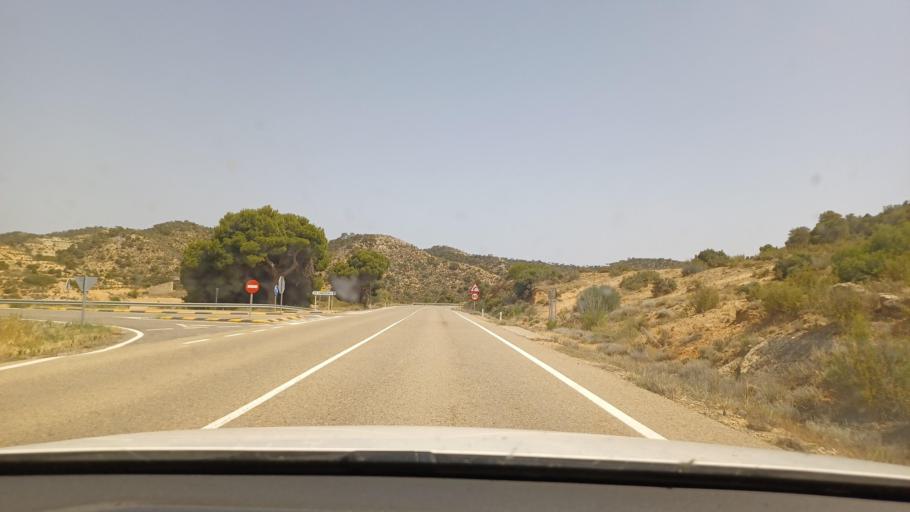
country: ES
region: Aragon
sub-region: Provincia de Zaragoza
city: Chiprana
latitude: 41.3465
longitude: -0.0887
